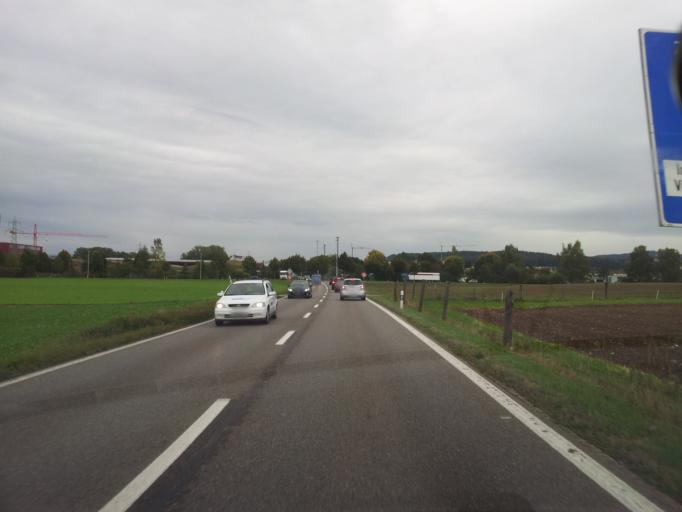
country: CH
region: Aargau
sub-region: Bezirk Bremgarten
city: Villmergen
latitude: 47.3579
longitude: 8.2437
